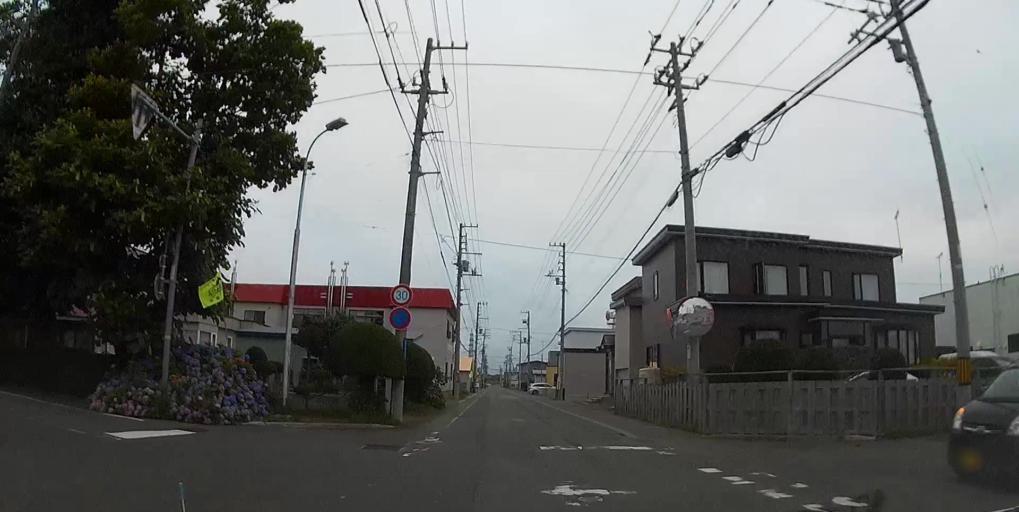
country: JP
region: Hokkaido
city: Nanae
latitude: 42.2585
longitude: 140.2702
